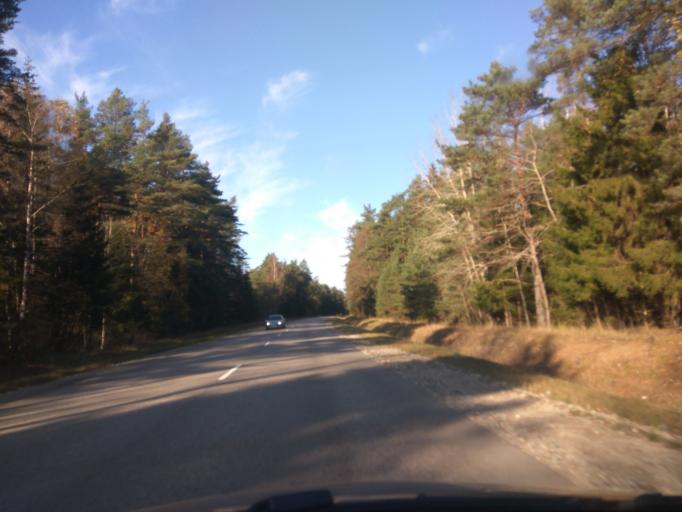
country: LV
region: Ventspils Rajons
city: Piltene
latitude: 57.0818
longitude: 21.7836
